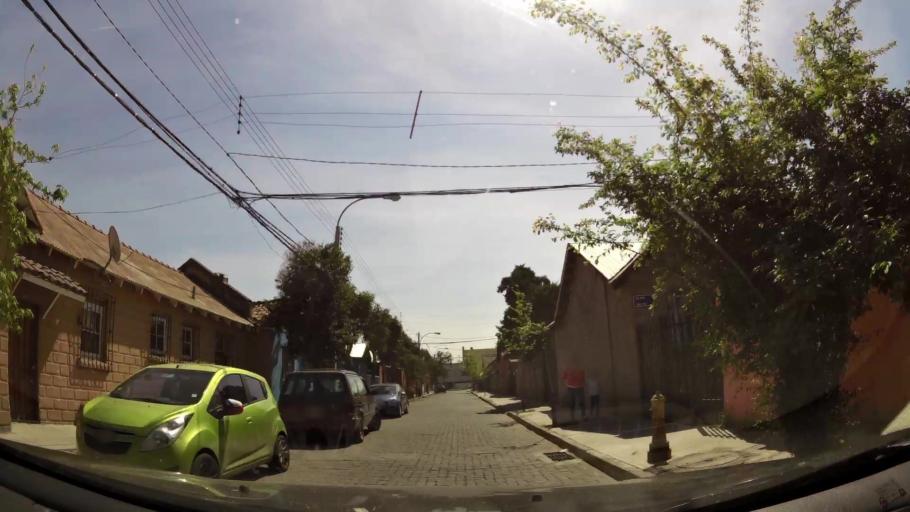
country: CL
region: Santiago Metropolitan
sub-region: Provincia de Cordillera
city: Puente Alto
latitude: -33.6130
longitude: -70.5677
